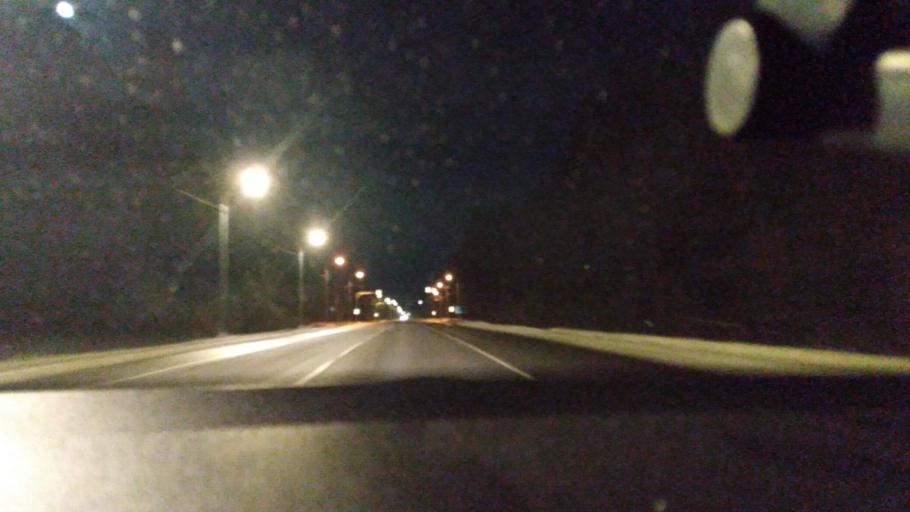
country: RU
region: Moskovskaya
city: Il'inskiy Pogost
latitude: 55.4602
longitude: 38.9840
